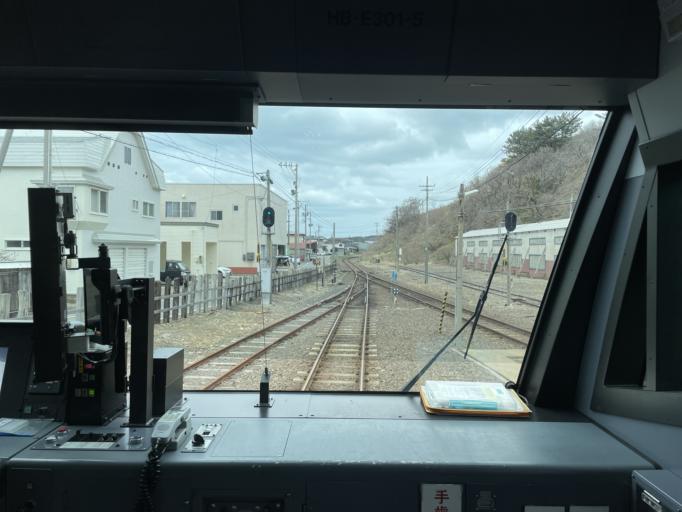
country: JP
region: Akita
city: Noshiromachi
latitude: 40.6508
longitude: 139.9297
